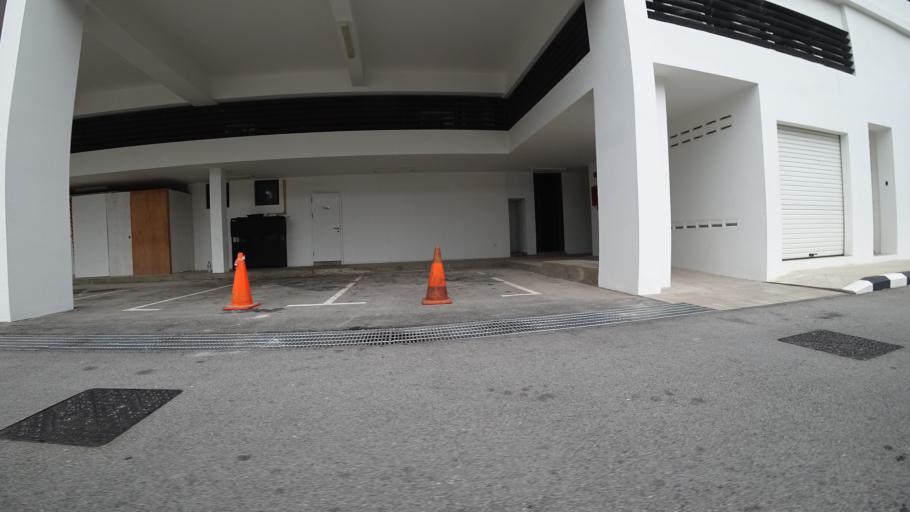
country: BN
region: Brunei and Muara
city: Bandar Seri Begawan
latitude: 4.9050
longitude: 114.9289
